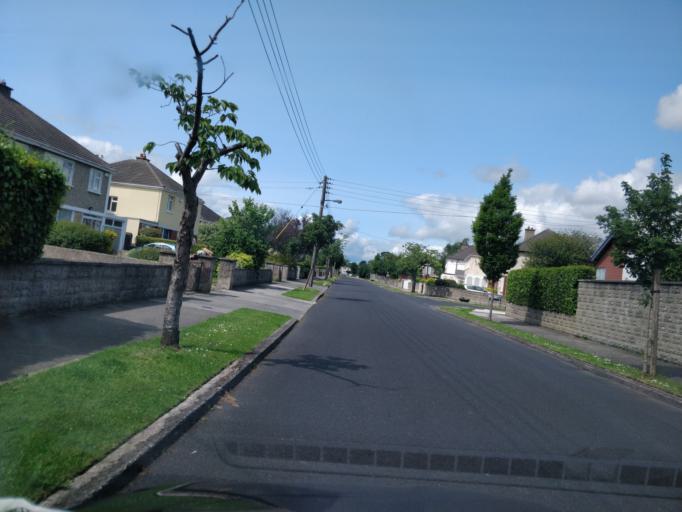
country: IE
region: Leinster
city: Dundrum
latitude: 53.2833
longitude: -6.2524
